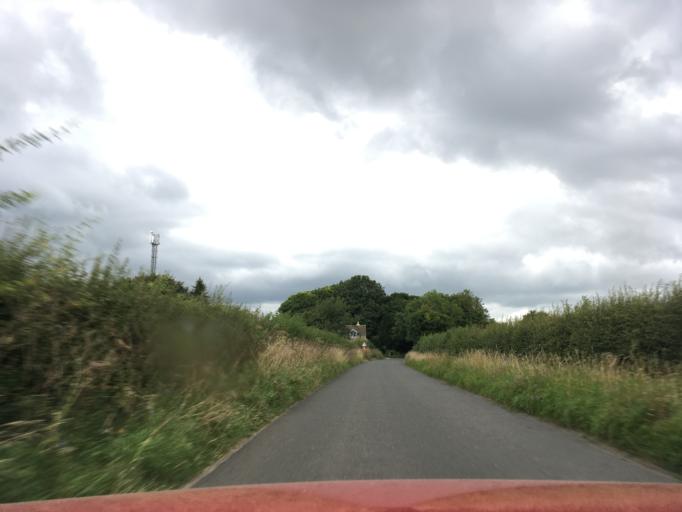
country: GB
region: England
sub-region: Gloucestershire
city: Chalford
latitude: 51.7741
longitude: -2.0937
